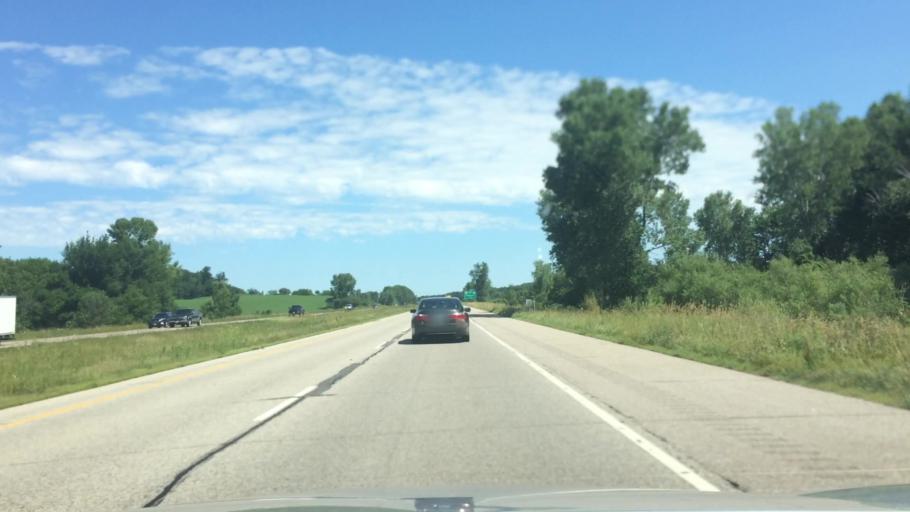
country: US
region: Wisconsin
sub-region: Columbia County
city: Portage
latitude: 43.6788
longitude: -89.4697
